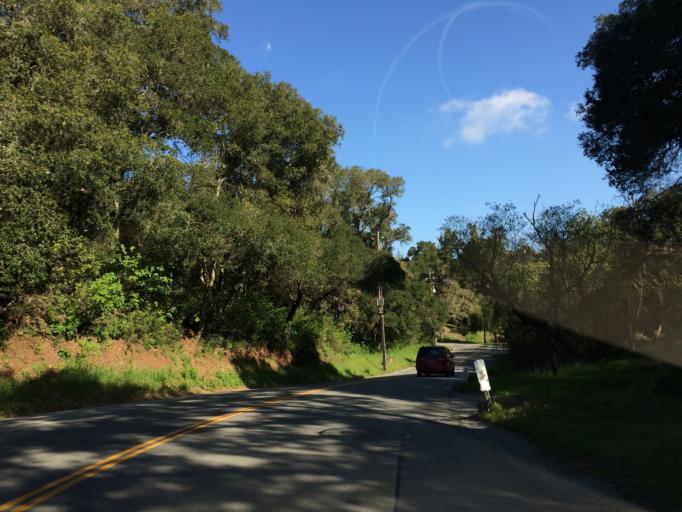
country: US
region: California
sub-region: Santa Clara County
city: Los Altos Hills
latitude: 37.3756
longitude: -122.1667
